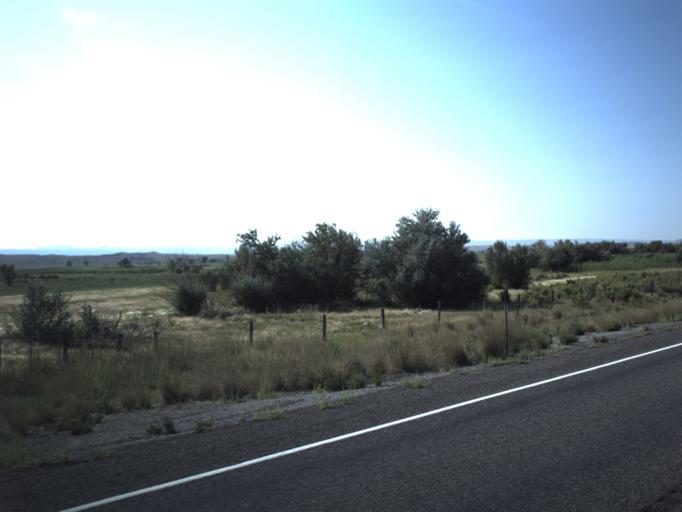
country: US
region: Utah
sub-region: Emery County
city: Castle Dale
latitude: 39.2356
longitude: -110.9921
